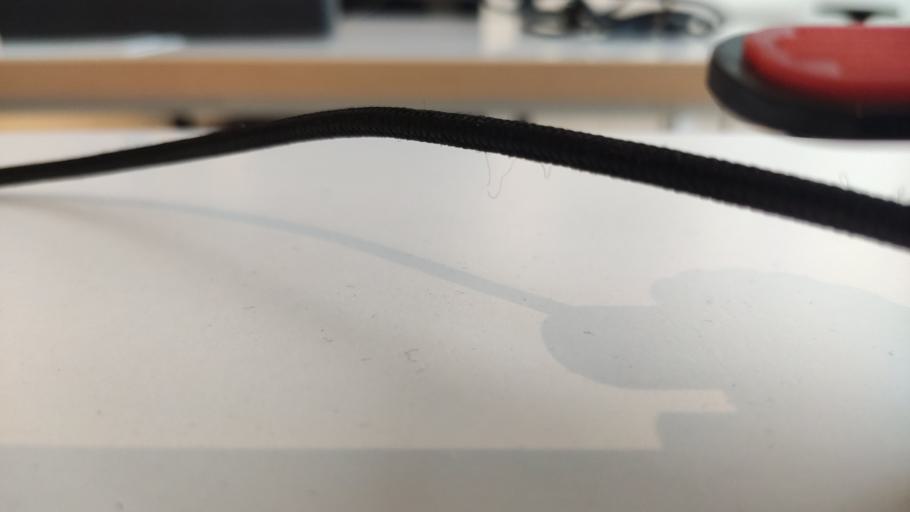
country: RU
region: Moskovskaya
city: Klin
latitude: 56.3642
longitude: 36.7653
